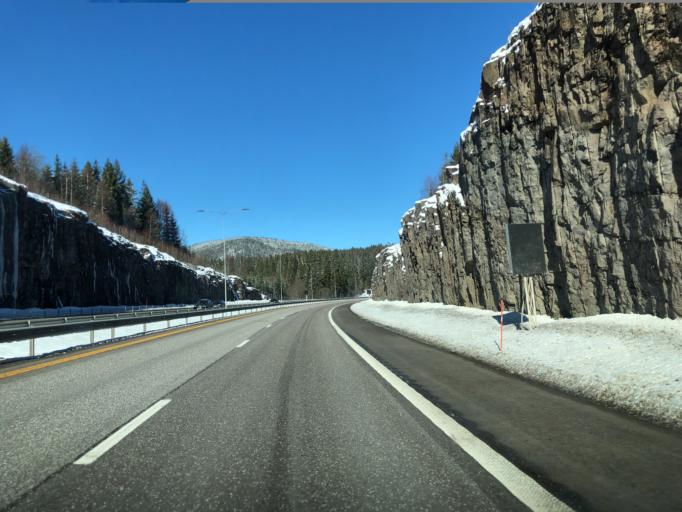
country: NO
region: Vestfold
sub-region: Sande
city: Sande
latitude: 59.5953
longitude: 10.1671
